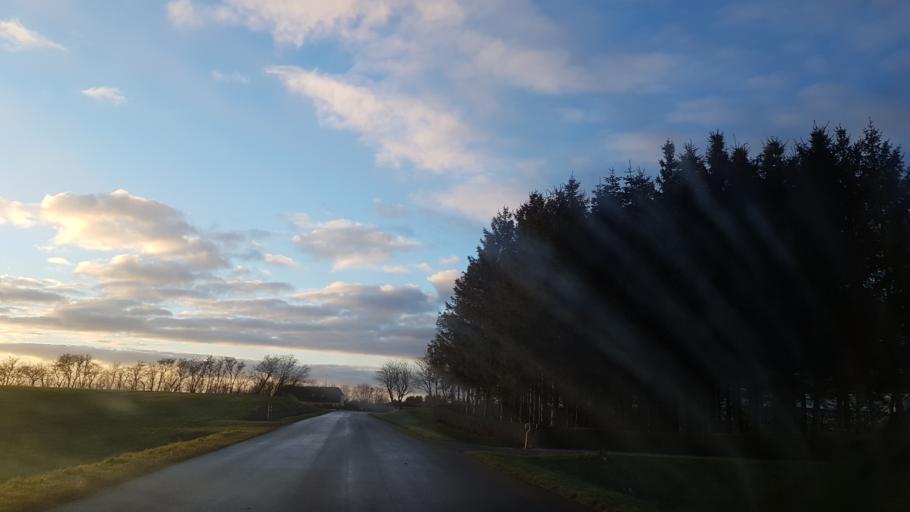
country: DK
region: South Denmark
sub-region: Kolding Kommune
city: Vamdrup
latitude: 55.3743
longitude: 9.2904
